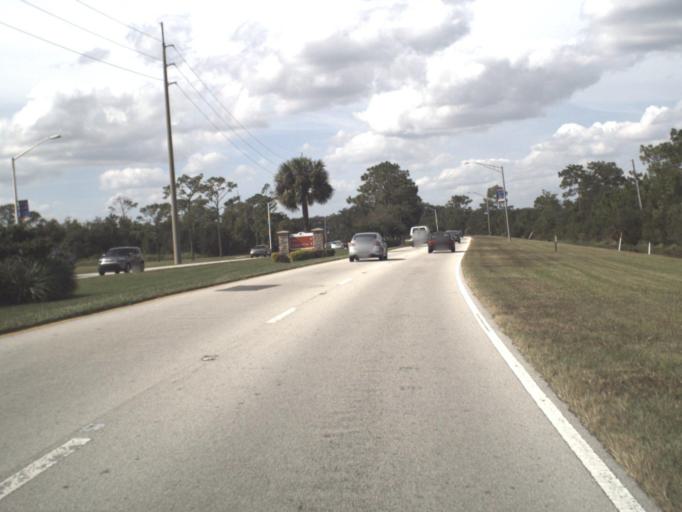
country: US
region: Florida
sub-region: Osceola County
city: Poinciana
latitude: 28.1458
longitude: -81.4592
